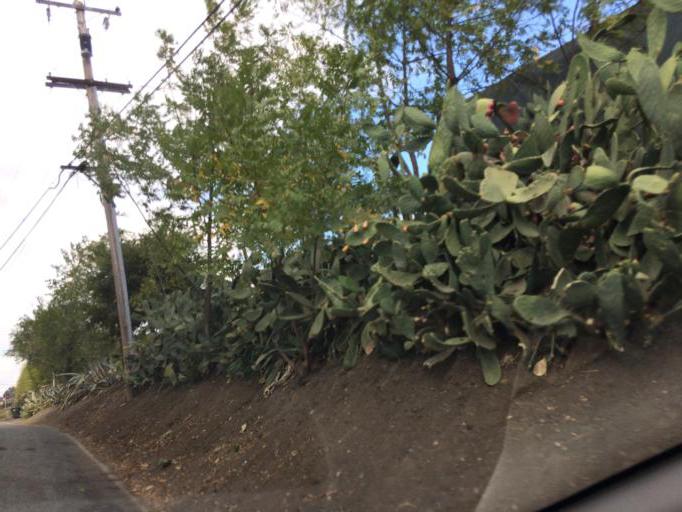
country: US
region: California
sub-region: Santa Clara County
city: East Foothills
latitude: 37.3822
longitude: -121.7993
